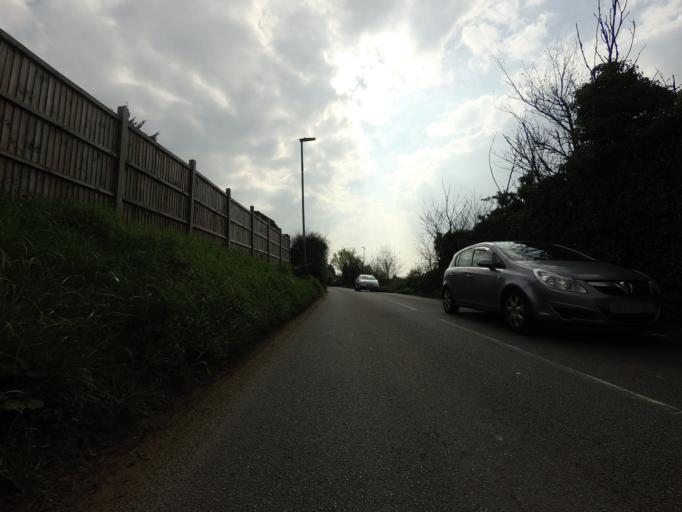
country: GB
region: England
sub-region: Greater London
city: Sidcup
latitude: 51.4093
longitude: 0.1242
